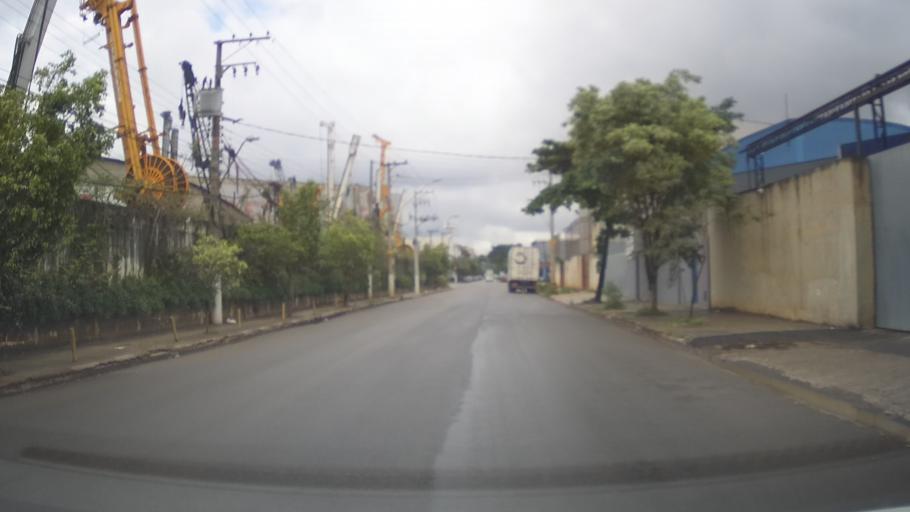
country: BR
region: Sao Paulo
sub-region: Guarulhos
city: Guarulhos
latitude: -23.4646
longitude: -46.4865
